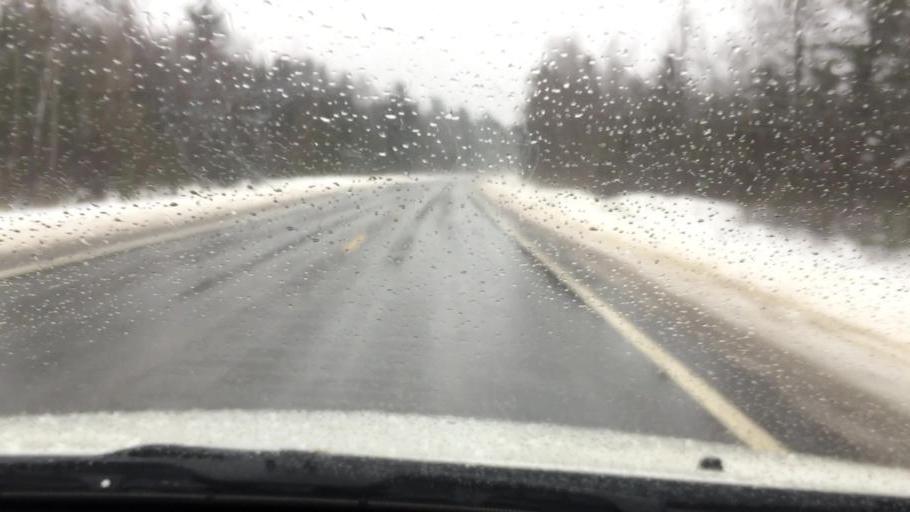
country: US
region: Michigan
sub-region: Charlevoix County
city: East Jordan
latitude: 45.0562
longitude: -85.0739
